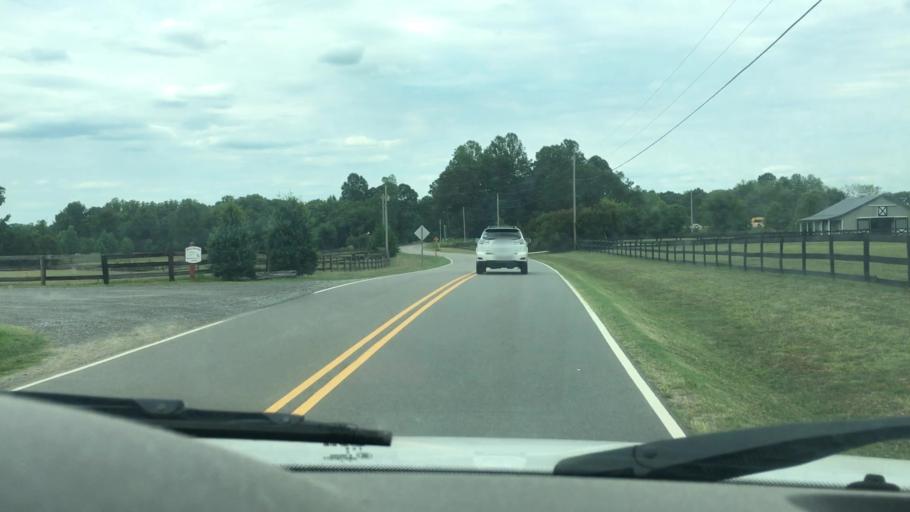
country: US
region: North Carolina
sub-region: Gaston County
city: Davidson
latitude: 35.4588
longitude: -80.7940
